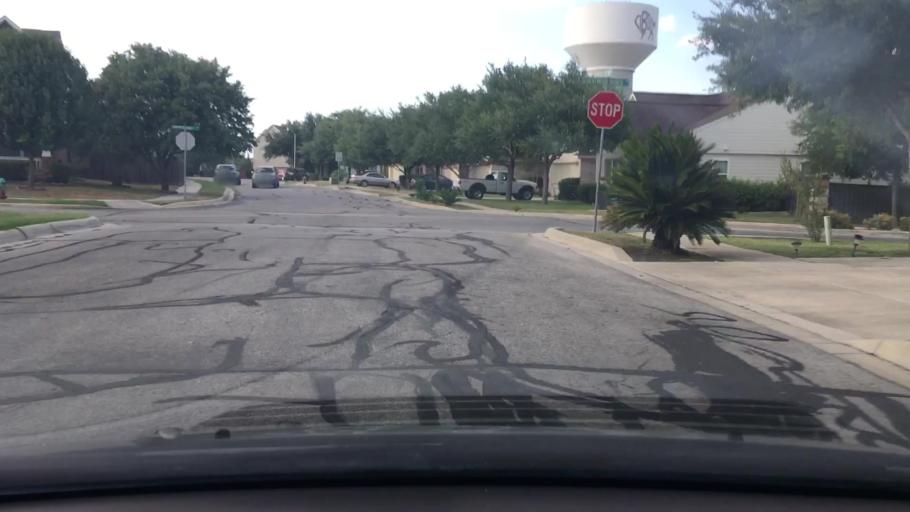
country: US
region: Texas
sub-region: Guadalupe County
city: Cibolo
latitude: 29.5825
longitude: -98.2471
